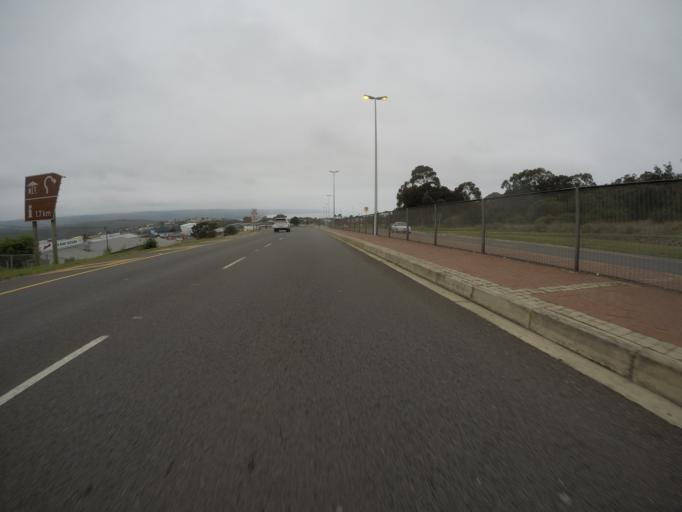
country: ZA
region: Western Cape
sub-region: Eden District Municipality
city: Plettenberg Bay
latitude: -34.0508
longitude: 23.3548
